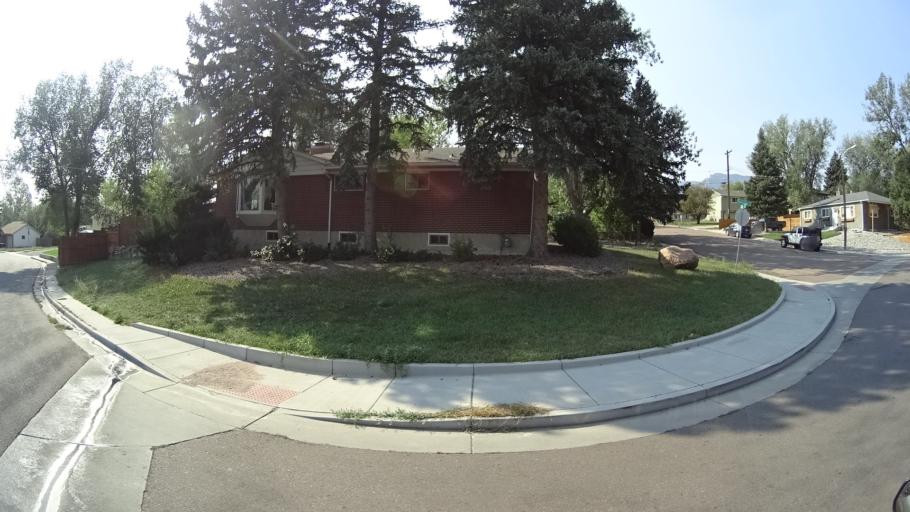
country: US
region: Colorado
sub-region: El Paso County
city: Colorado Springs
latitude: 38.8092
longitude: -104.8365
